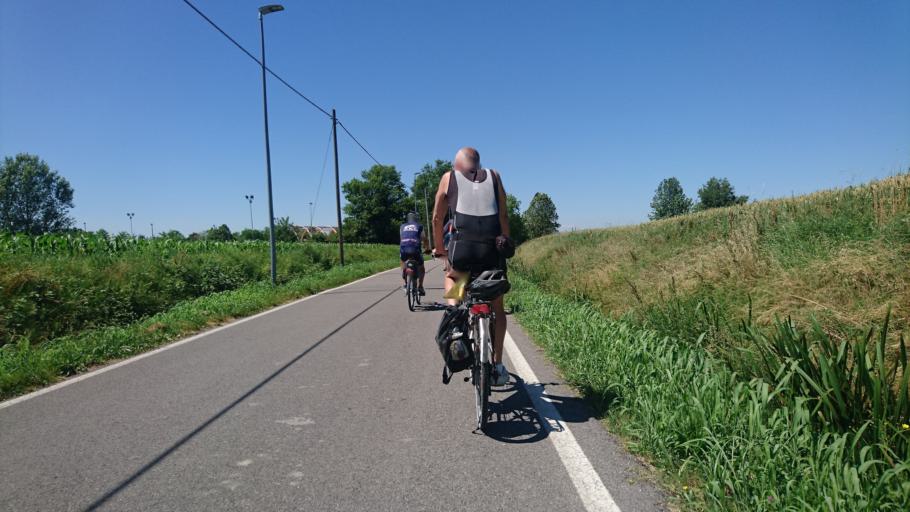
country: IT
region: Veneto
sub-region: Provincia di Padova
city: Bertipaglia
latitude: 45.3077
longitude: 11.8873
